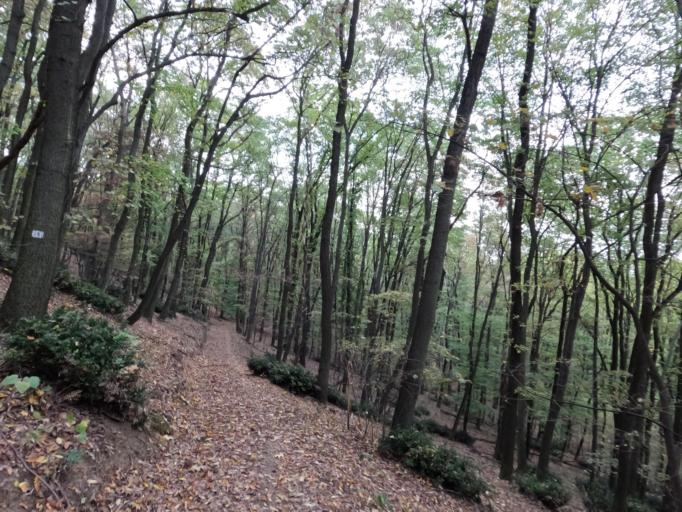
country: HU
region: Tolna
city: Szentgalpuszta
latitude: 46.3265
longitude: 18.6168
